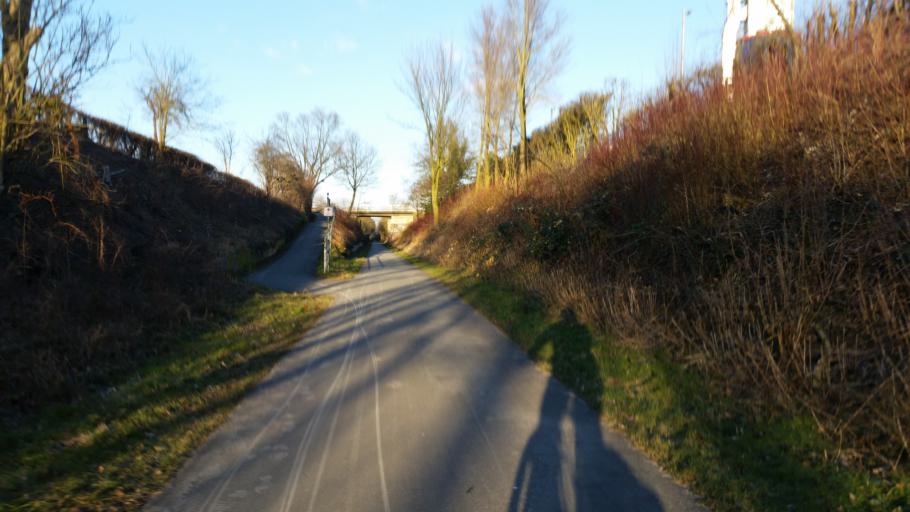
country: DE
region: North Rhine-Westphalia
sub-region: Regierungsbezirk Munster
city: Neuenkirchen
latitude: 52.2513
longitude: 7.3767
